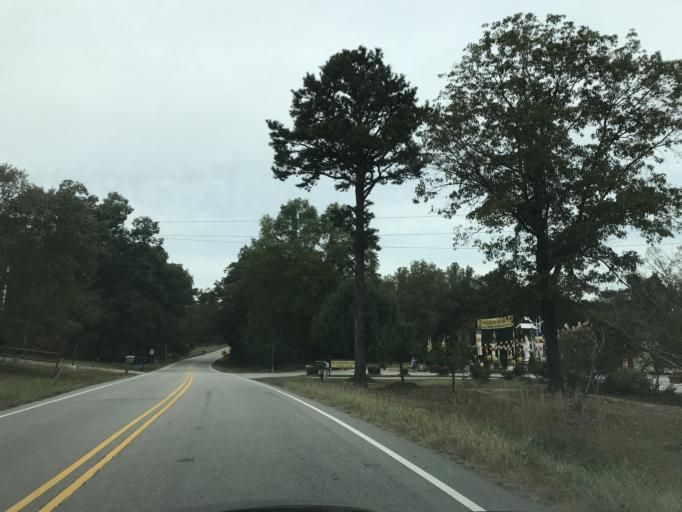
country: US
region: North Carolina
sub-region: Wake County
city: Rolesville
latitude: 35.8633
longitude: -78.5140
